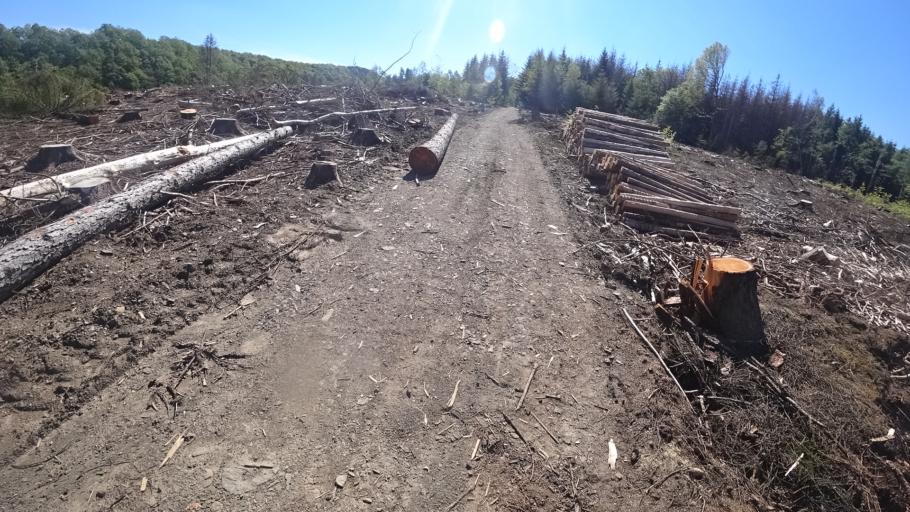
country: DE
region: Rheinland-Pfalz
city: Kausen
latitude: 50.7362
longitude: 7.8600
